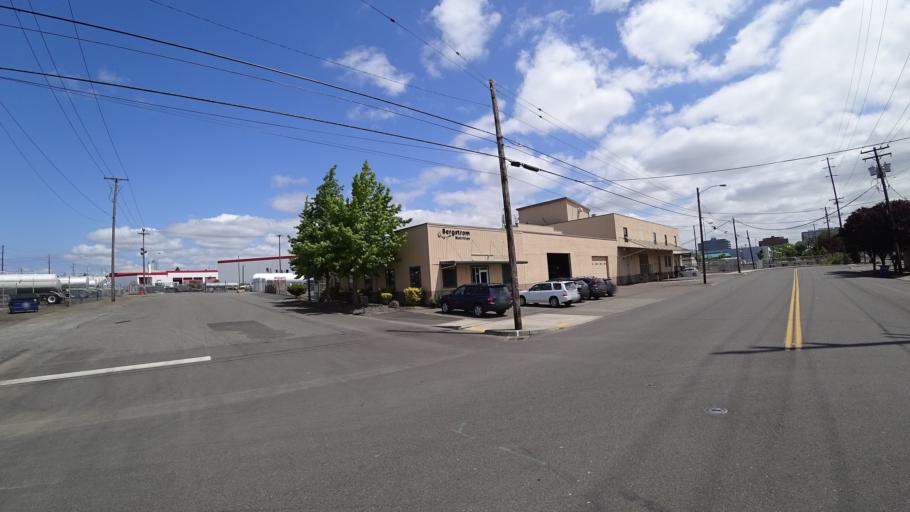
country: US
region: Washington
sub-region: Clark County
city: Vancouver
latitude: 45.6273
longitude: -122.6826
